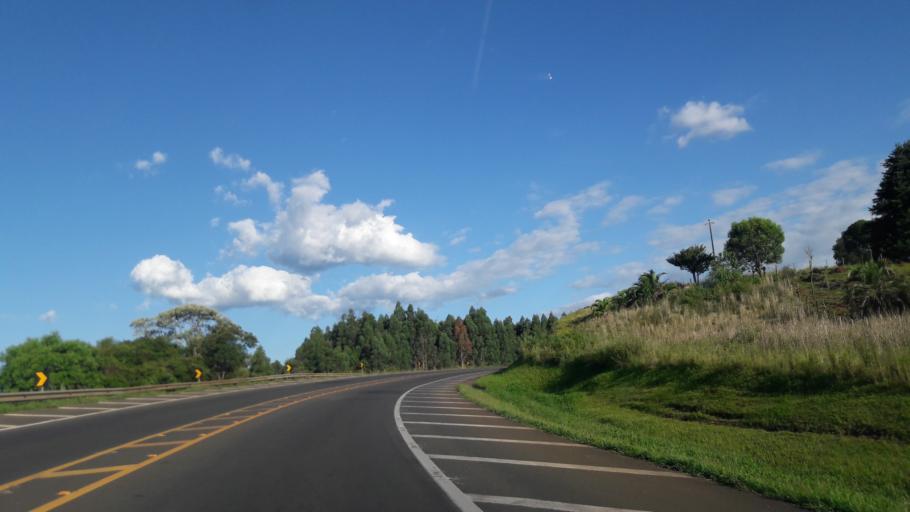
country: BR
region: Parana
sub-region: Guarapuava
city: Guarapuava
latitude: -25.3660
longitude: -51.3426
